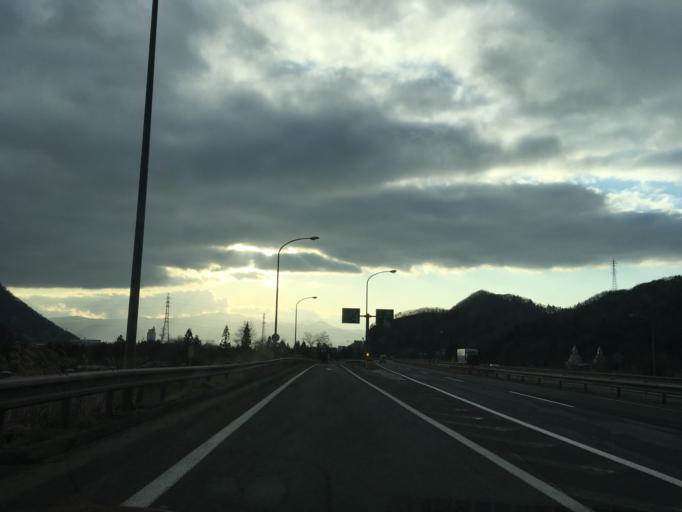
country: JP
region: Yamagata
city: Yamagata-shi
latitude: 38.2447
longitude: 140.3864
